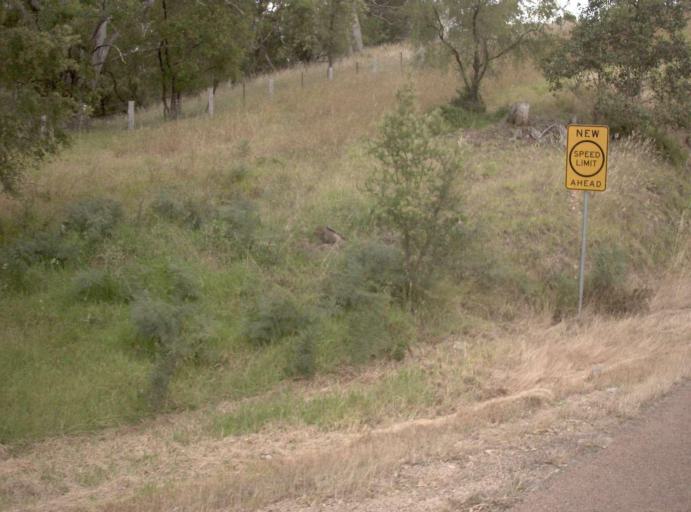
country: AU
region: Victoria
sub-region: East Gippsland
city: Bairnsdale
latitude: -37.8901
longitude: 147.6592
